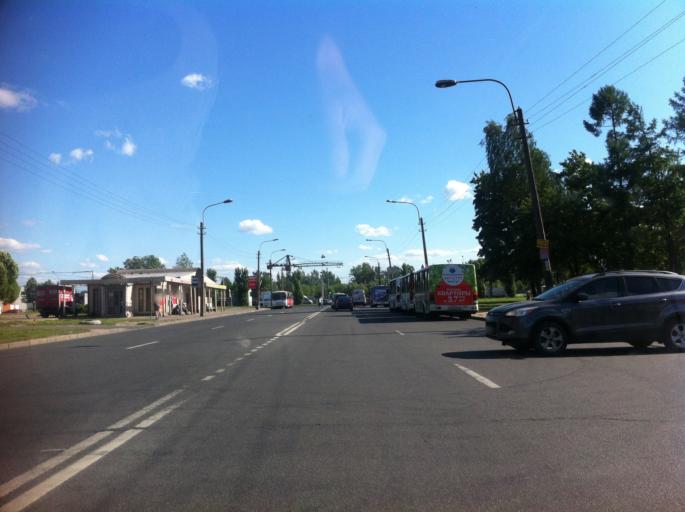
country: RU
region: St.-Petersburg
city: Uritsk
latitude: 59.8255
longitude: 30.1758
